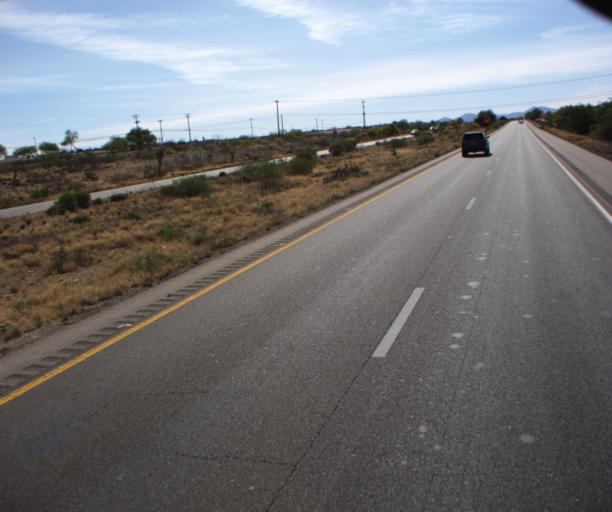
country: US
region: Arizona
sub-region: Pima County
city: Vail
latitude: 32.0139
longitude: -110.7010
